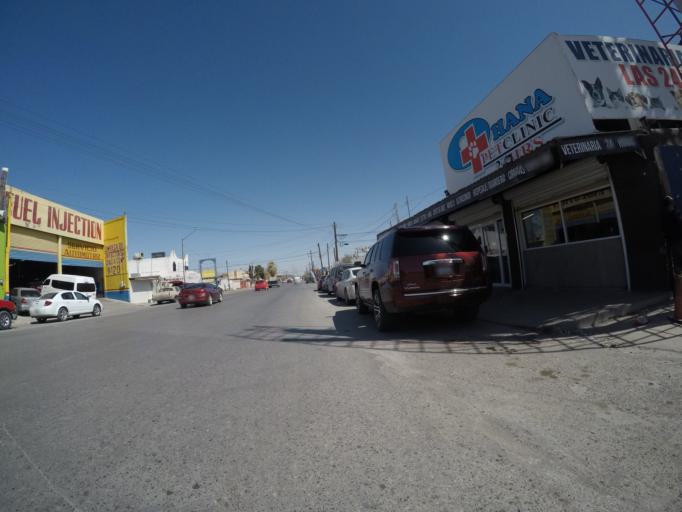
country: MX
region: Chihuahua
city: Ciudad Juarez
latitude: 31.7066
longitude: -106.4471
